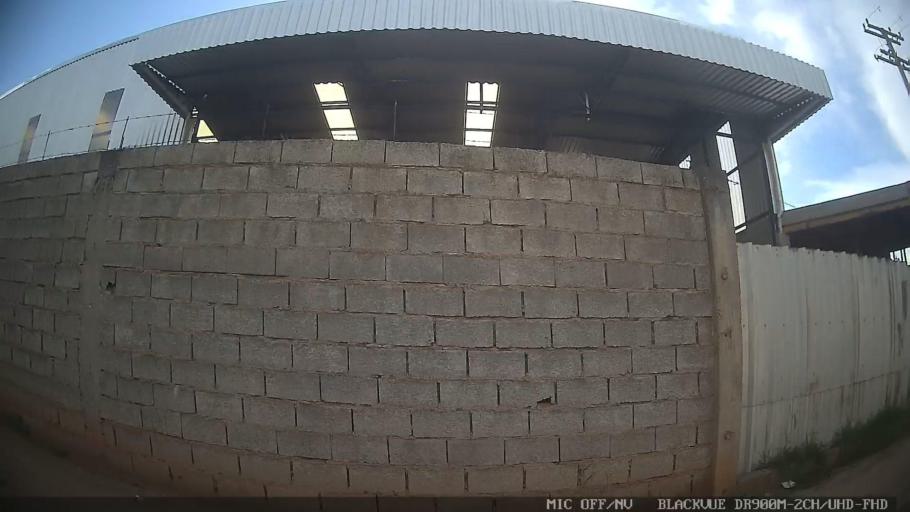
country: BR
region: Sao Paulo
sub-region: Bom Jesus Dos Perdoes
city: Bom Jesus dos Perdoes
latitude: -23.1222
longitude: -46.4831
